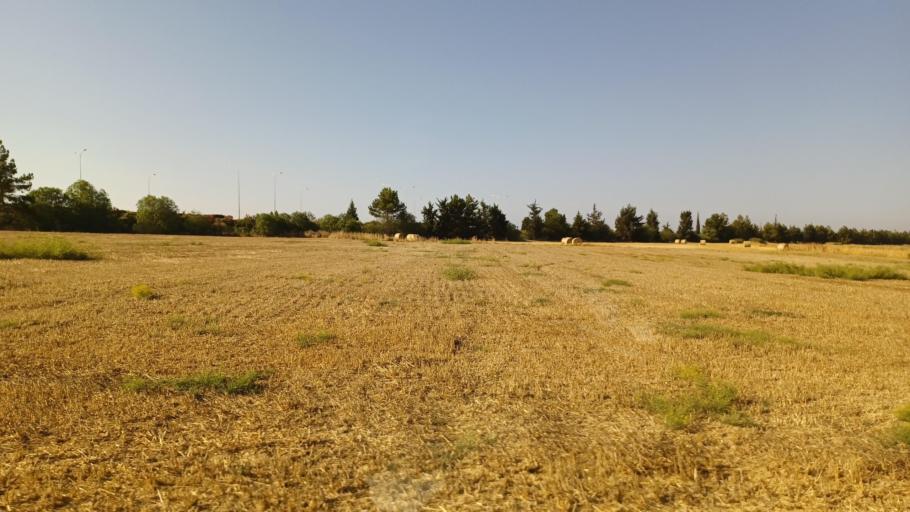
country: CY
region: Larnaka
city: Pyla
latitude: 34.9914
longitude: 33.6932
